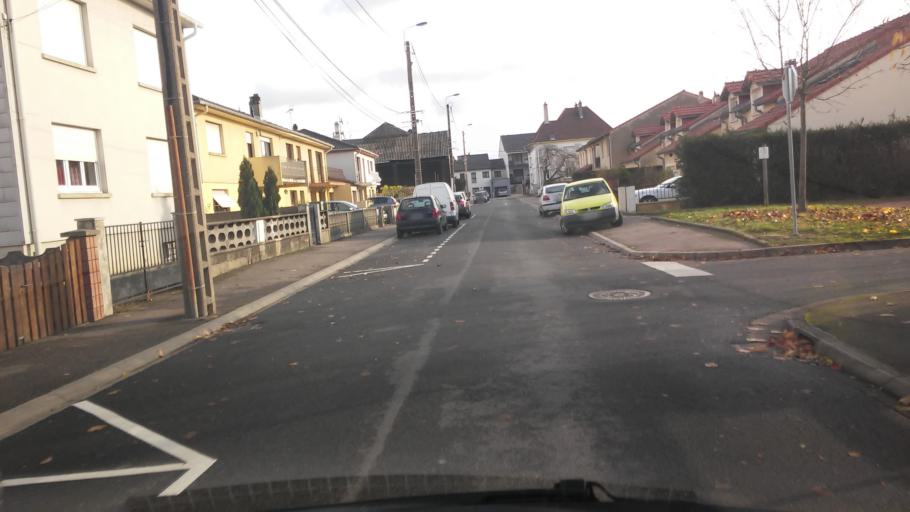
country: FR
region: Lorraine
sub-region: Departement de la Moselle
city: Talange
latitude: 49.2358
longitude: 6.1650
